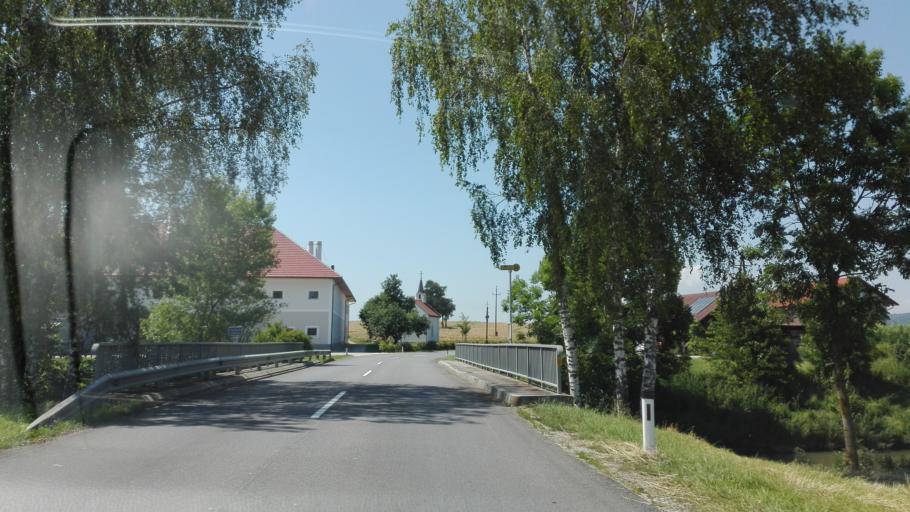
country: AT
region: Upper Austria
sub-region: Politischer Bezirk Grieskirchen
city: Grieskirchen
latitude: 48.3463
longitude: 13.8693
